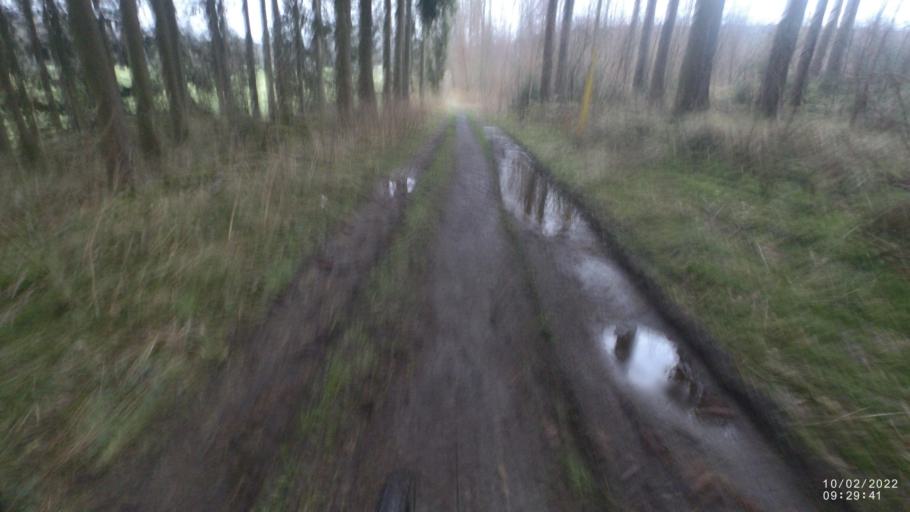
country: DE
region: North Rhine-Westphalia
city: Kierspe
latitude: 51.1809
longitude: 7.5779
